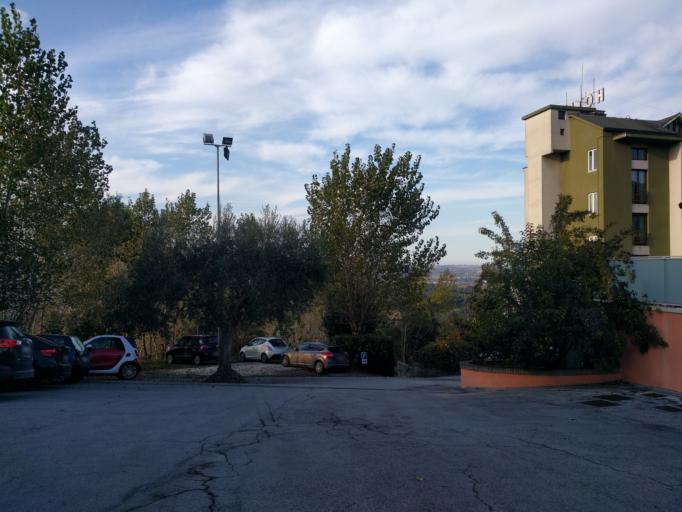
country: IT
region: The Marches
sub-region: Provincia di Ancona
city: Ostra
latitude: 43.6112
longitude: 13.1532
